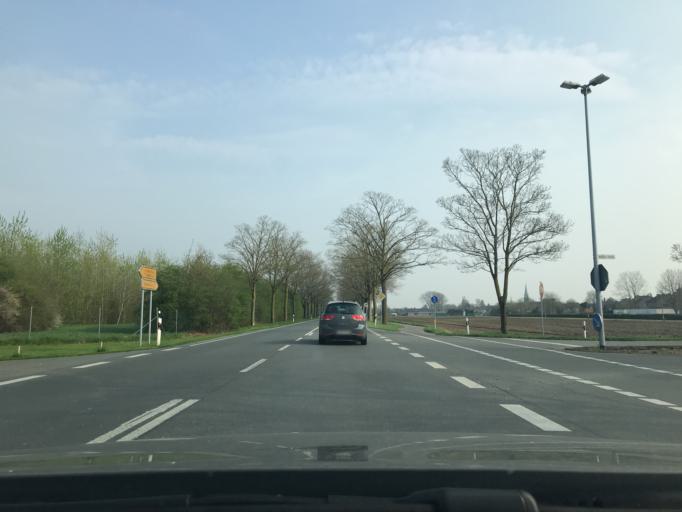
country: DE
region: North Rhine-Westphalia
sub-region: Regierungsbezirk Dusseldorf
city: Kevelaer
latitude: 51.5966
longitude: 6.2353
